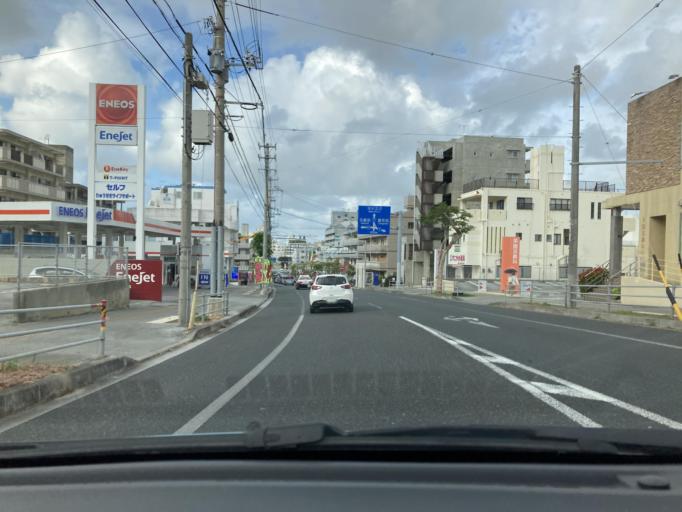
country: JP
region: Okinawa
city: Tomigusuku
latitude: 26.1907
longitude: 127.6750
